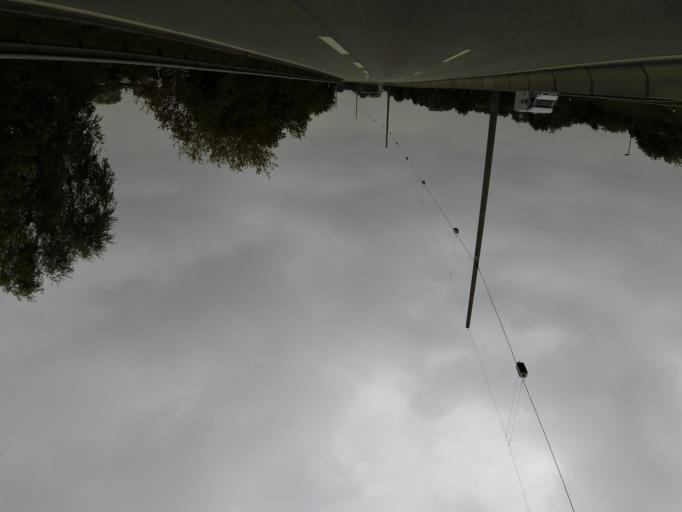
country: DE
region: Hamburg
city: Eidelstedt
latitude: 53.6211
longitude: 9.9028
